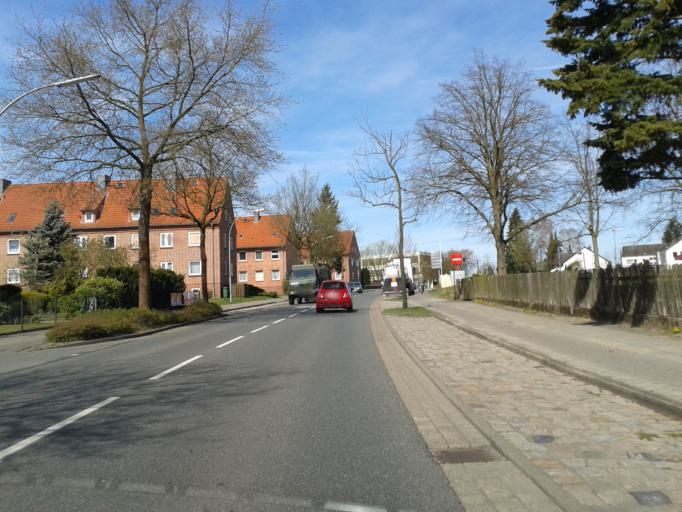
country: DE
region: Lower Saxony
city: Munster
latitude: 52.9815
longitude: 10.0888
